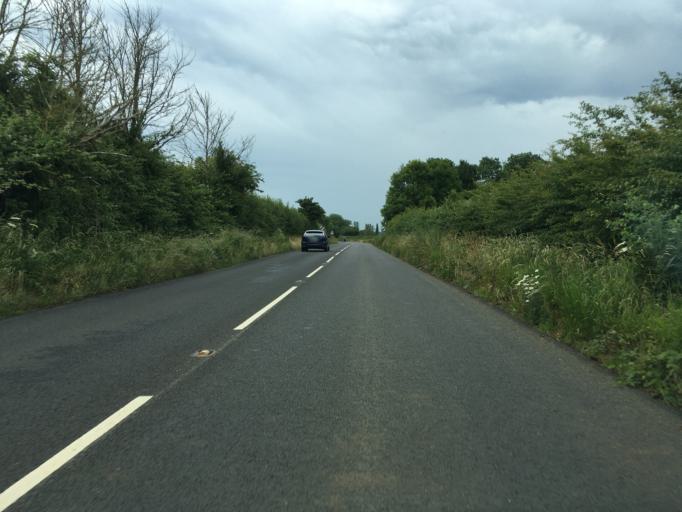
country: GB
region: England
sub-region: Gloucestershire
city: Stonehouse
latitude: 51.7844
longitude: -2.2895
